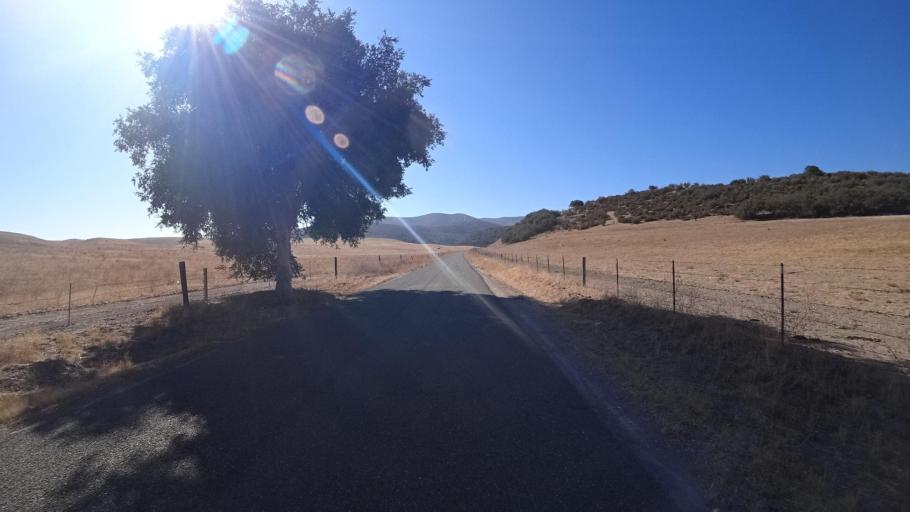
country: US
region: California
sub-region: Monterey County
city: King City
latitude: 36.0542
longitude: -121.0523
